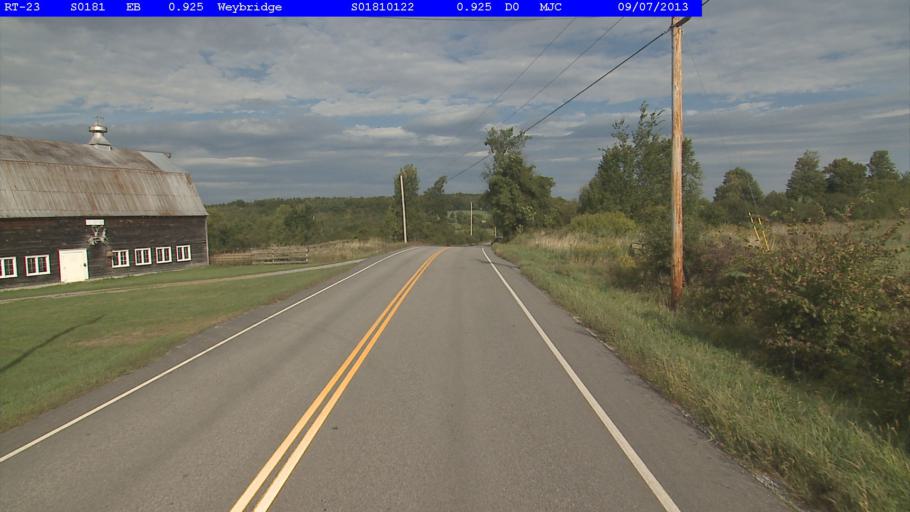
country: US
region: Vermont
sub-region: Addison County
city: Middlebury (village)
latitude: 44.0271
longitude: -73.1971
